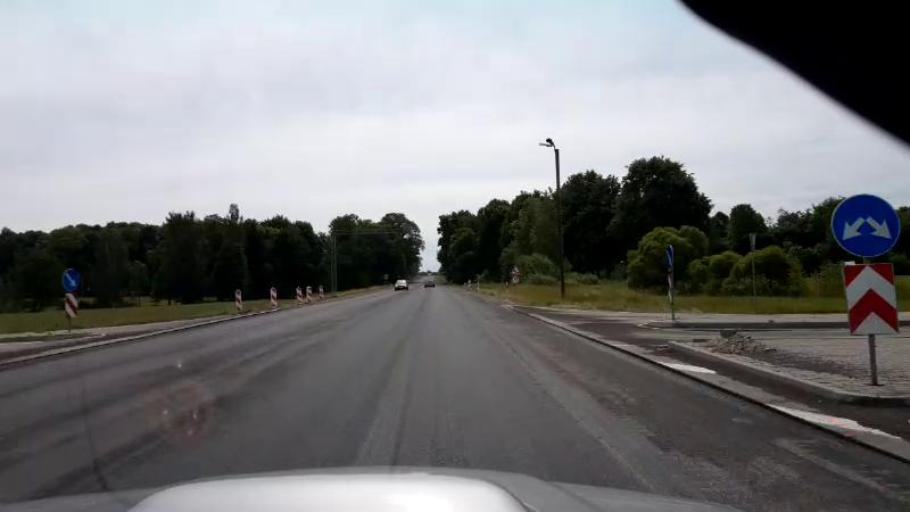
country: LV
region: Bauskas Rajons
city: Bauska
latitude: 56.3797
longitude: 24.2618
